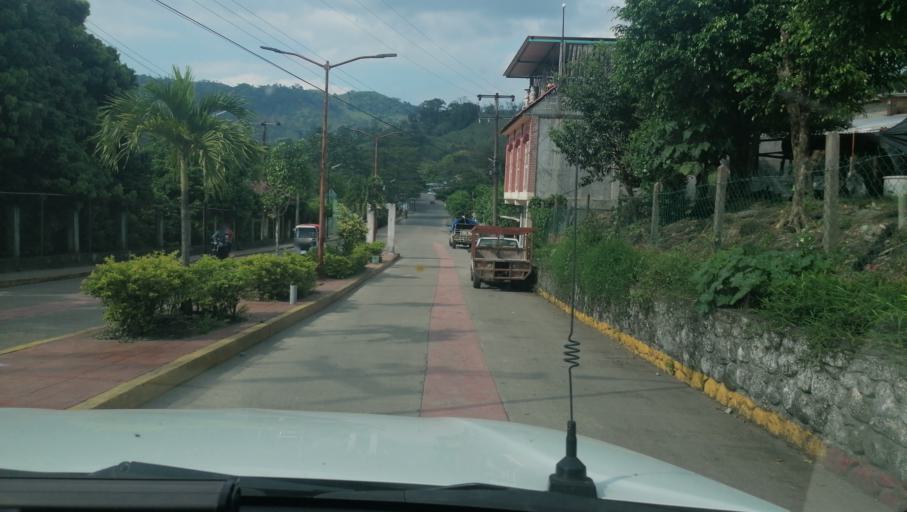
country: MX
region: Chiapas
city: Ostuacan
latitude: 17.4101
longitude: -93.3361
